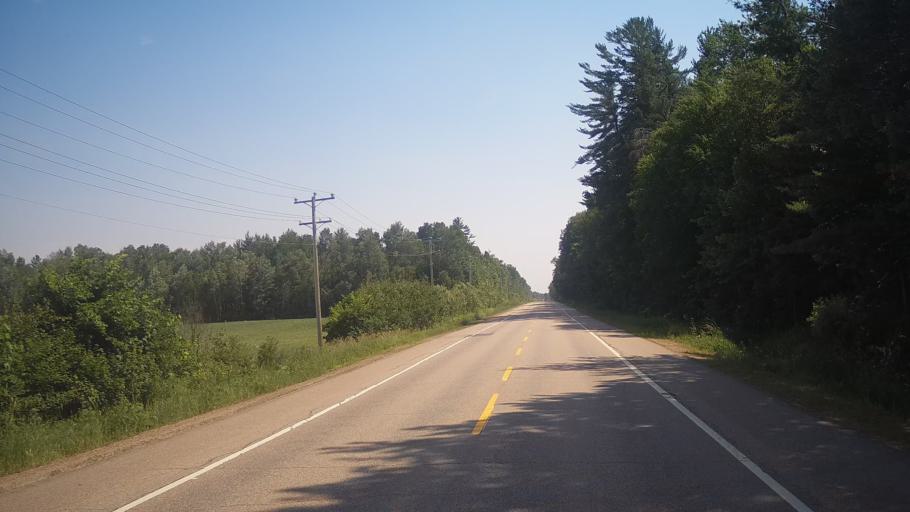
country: CA
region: Ontario
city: Pembroke
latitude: 45.8436
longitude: -77.0135
